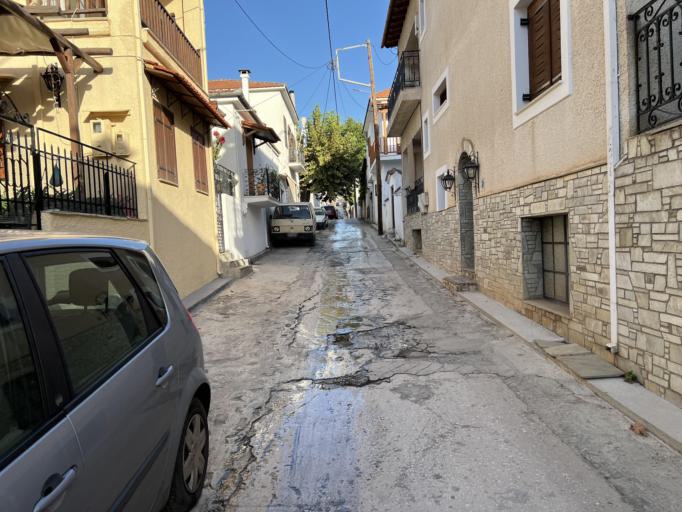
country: GR
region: Thessaly
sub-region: Nomos Magnisias
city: Sourpi
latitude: 39.1666
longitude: 22.8896
